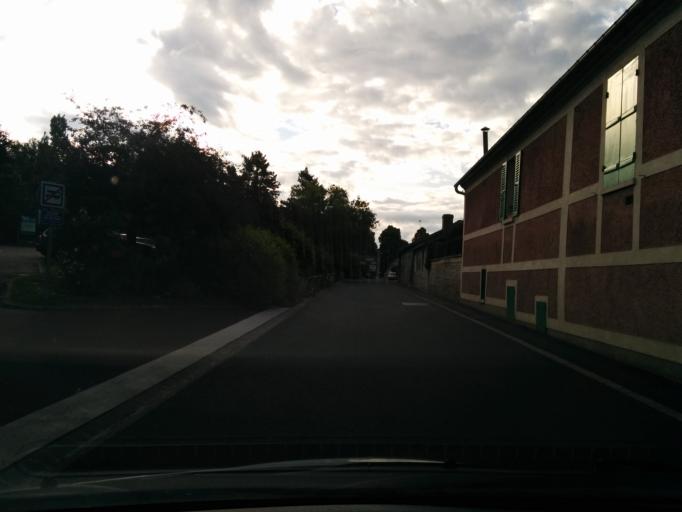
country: FR
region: Ile-de-France
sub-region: Departement des Yvelines
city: Limetz-Villez
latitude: 49.0754
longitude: 1.5338
